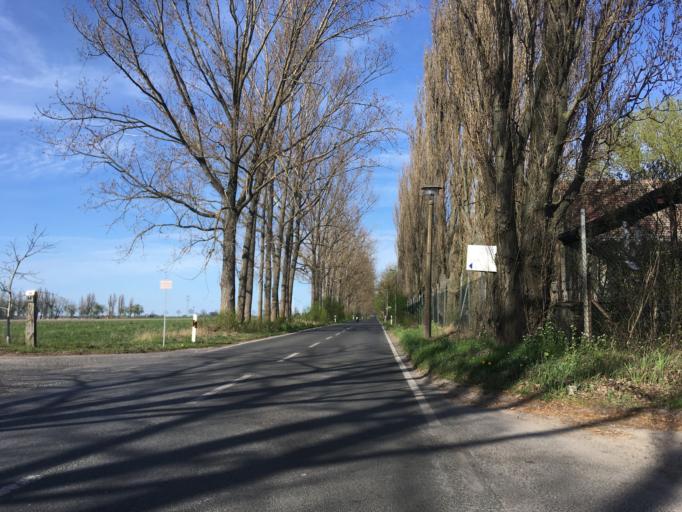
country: DE
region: Berlin
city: Wartenberg
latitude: 52.5836
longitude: 13.5225
